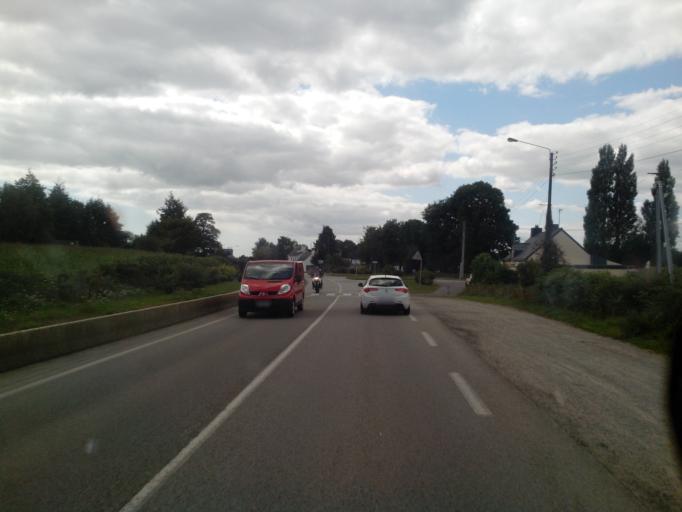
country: FR
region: Brittany
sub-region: Departement du Morbihan
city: Hennebont
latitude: 47.8161
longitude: -3.2404
